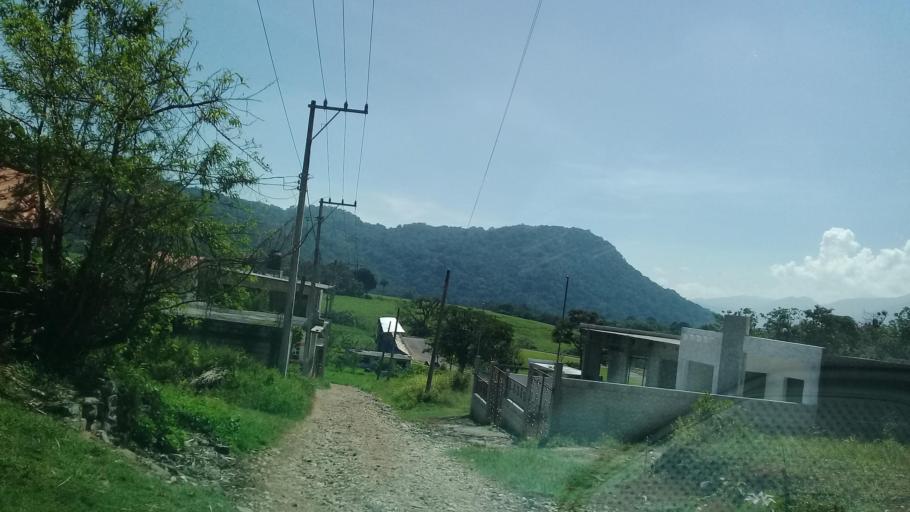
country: MX
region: Veracruz
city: Amatlan de los Reyes
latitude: 18.8444
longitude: -96.9115
